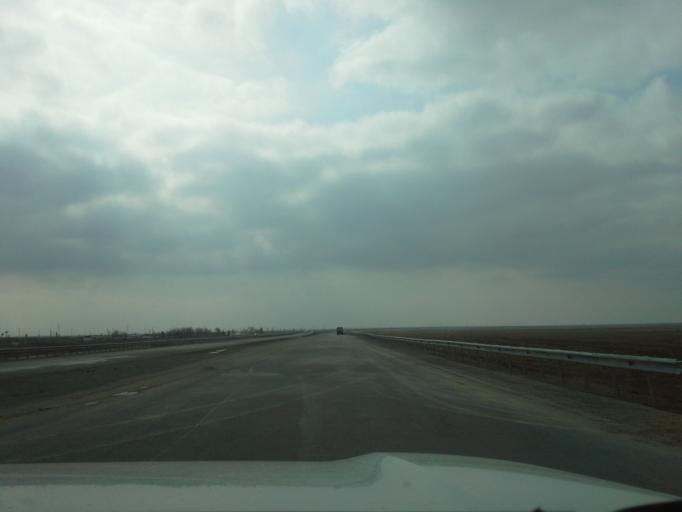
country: TM
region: Ahal
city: Tejen
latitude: 37.2287
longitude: 60.1436
